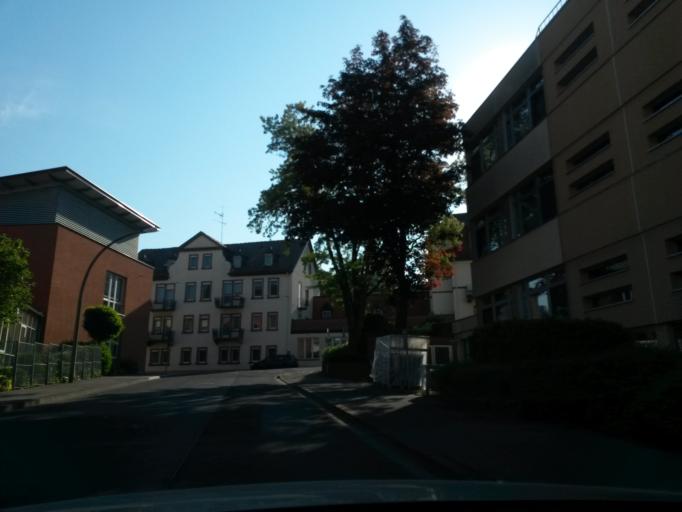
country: DE
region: Bavaria
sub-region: Regierungsbezirk Unterfranken
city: Bad Kissingen
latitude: 50.1980
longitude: 10.0817
